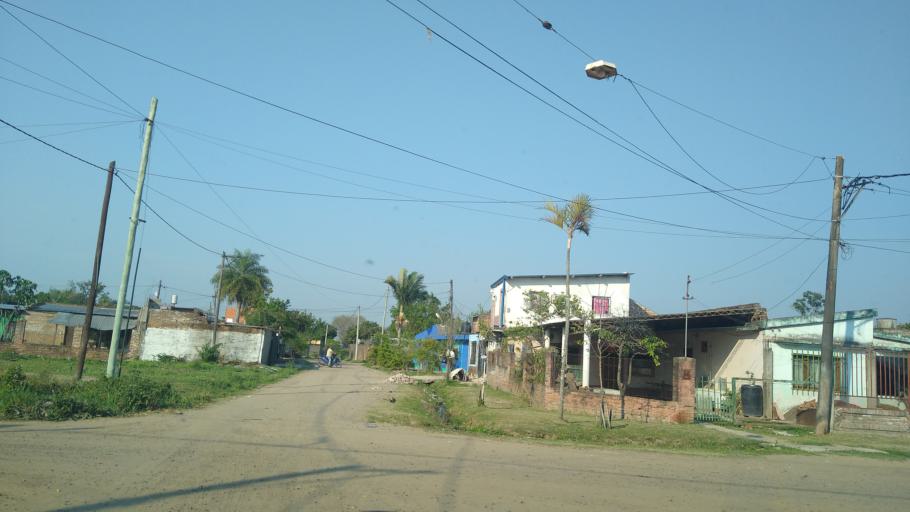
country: AR
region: Chaco
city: Barranqueras
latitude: -27.4773
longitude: -58.9282
